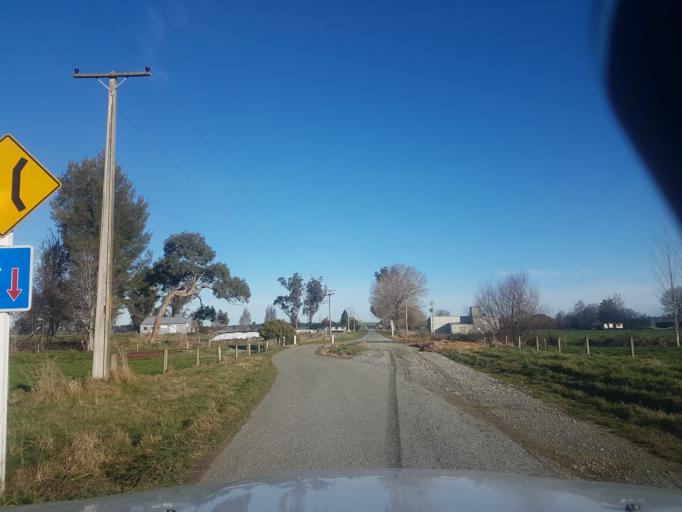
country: NZ
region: Canterbury
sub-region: Timaru District
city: Pleasant Point
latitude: -44.2630
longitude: 171.1733
